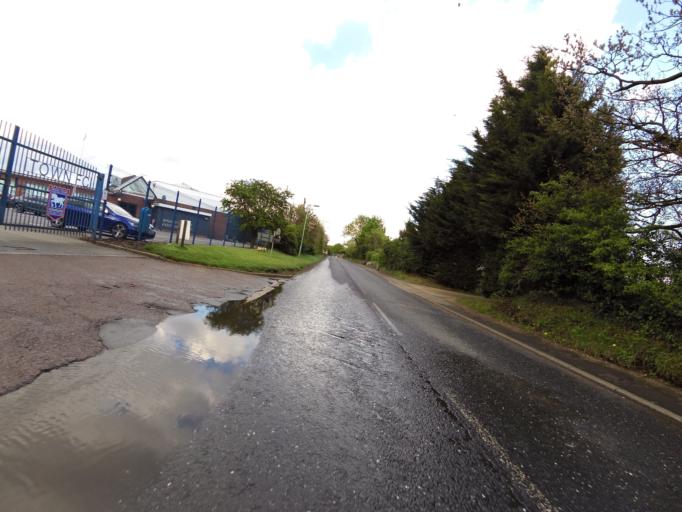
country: GB
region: England
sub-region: Suffolk
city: Kesgrave
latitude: 52.0660
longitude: 1.2130
